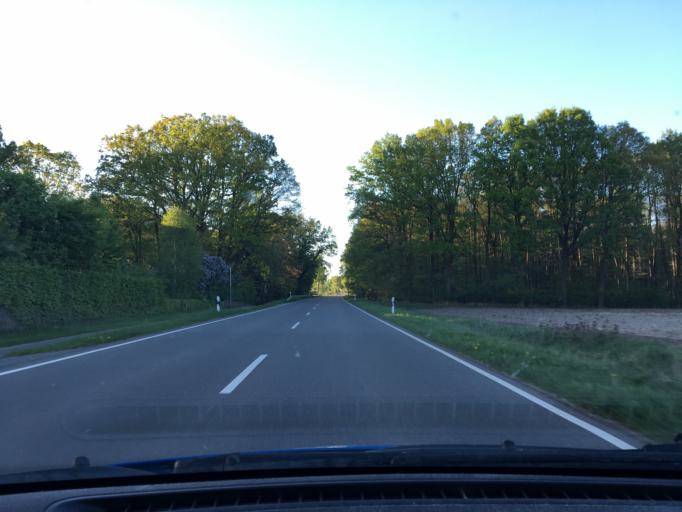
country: DE
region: Lower Saxony
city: Oldendorf
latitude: 53.1688
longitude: 10.2113
